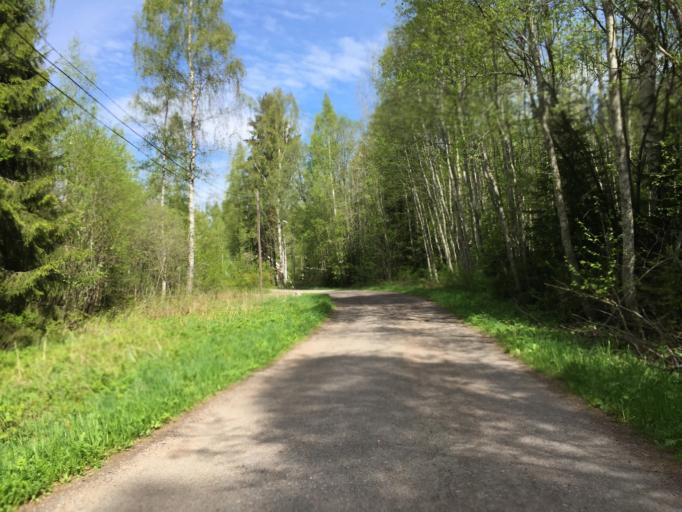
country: SE
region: Dalarna
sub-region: Ludvika Kommun
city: Ludvika
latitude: 60.1377
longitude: 15.1483
